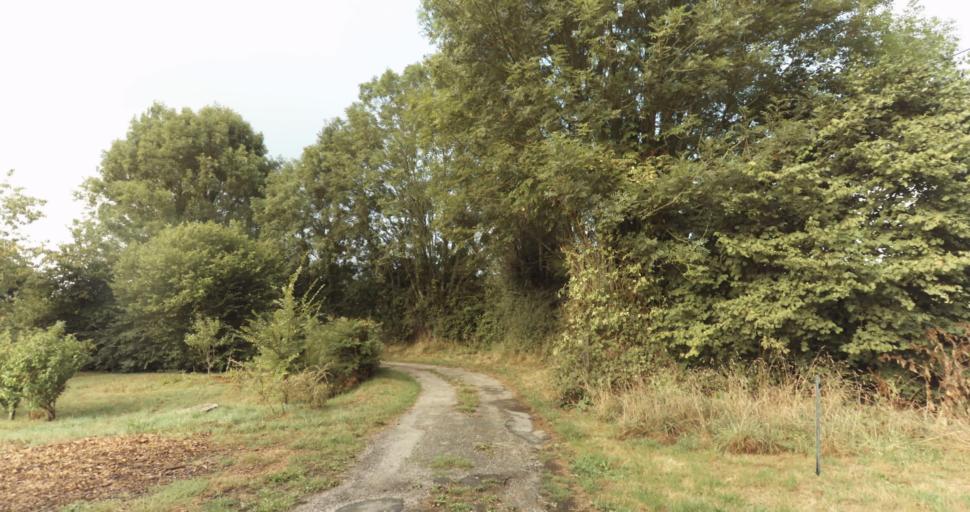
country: FR
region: Lower Normandy
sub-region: Departement de l'Orne
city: Gace
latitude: 48.8804
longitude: 0.2780
